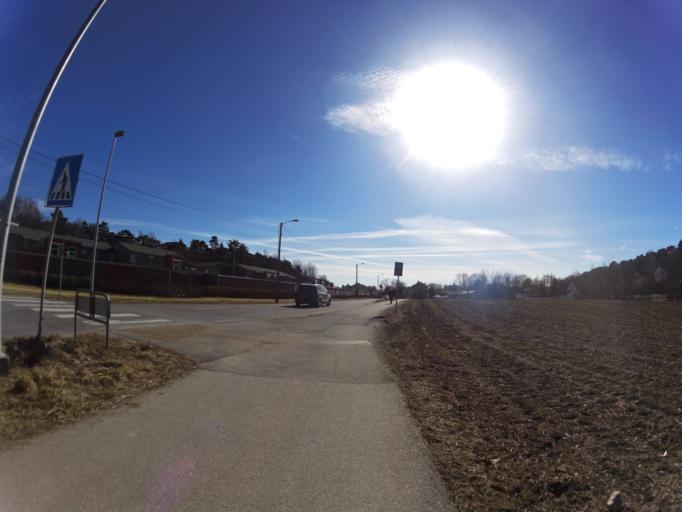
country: NO
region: Ostfold
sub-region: Fredrikstad
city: Fredrikstad
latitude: 59.2308
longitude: 10.9298
